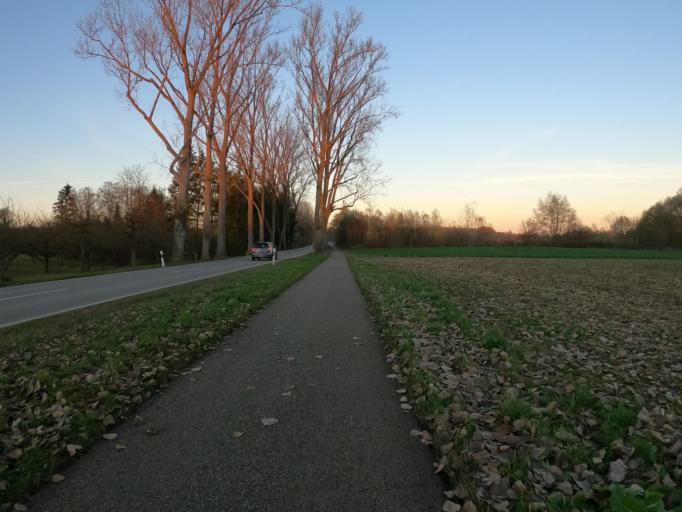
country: DE
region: Bavaria
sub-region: Swabia
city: Nersingen
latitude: 48.4258
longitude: 10.0814
